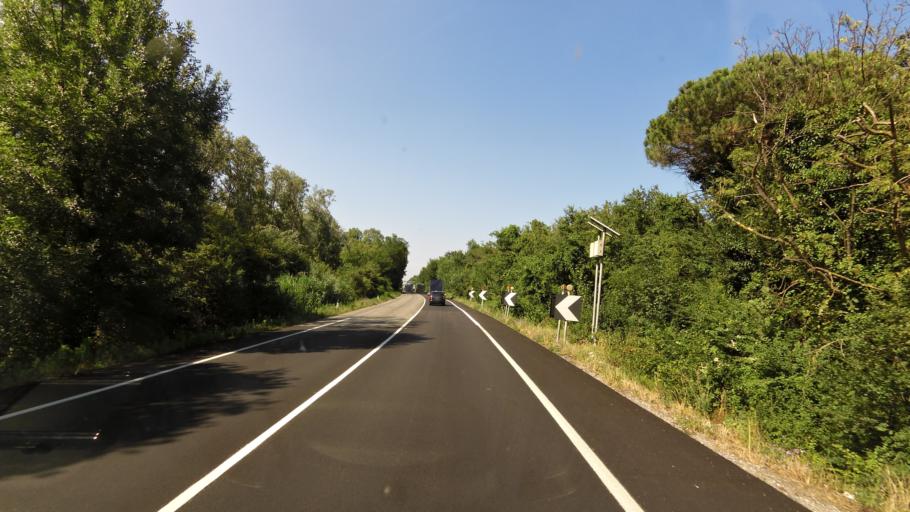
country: IT
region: Emilia-Romagna
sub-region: Provincia di Ravenna
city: Marina Romea
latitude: 44.5149
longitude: 12.2266
